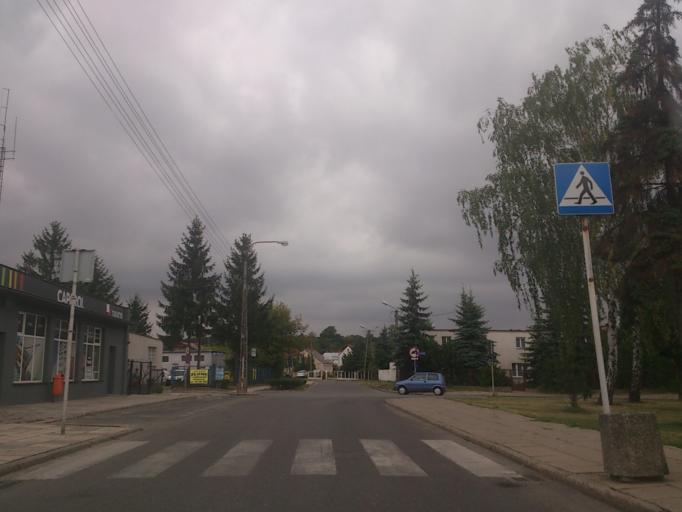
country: PL
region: Kujawsko-Pomorskie
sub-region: Powiat golubsko-dobrzynski
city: Golub-Dobrzyn
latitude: 53.1089
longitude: 19.0515
